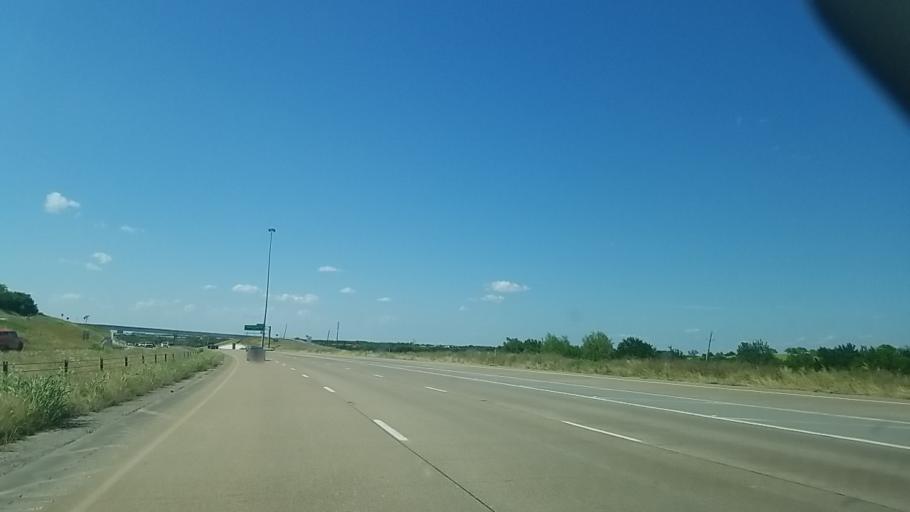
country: US
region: Texas
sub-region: Ellis County
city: Ferris
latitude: 32.5436
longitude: -96.6588
